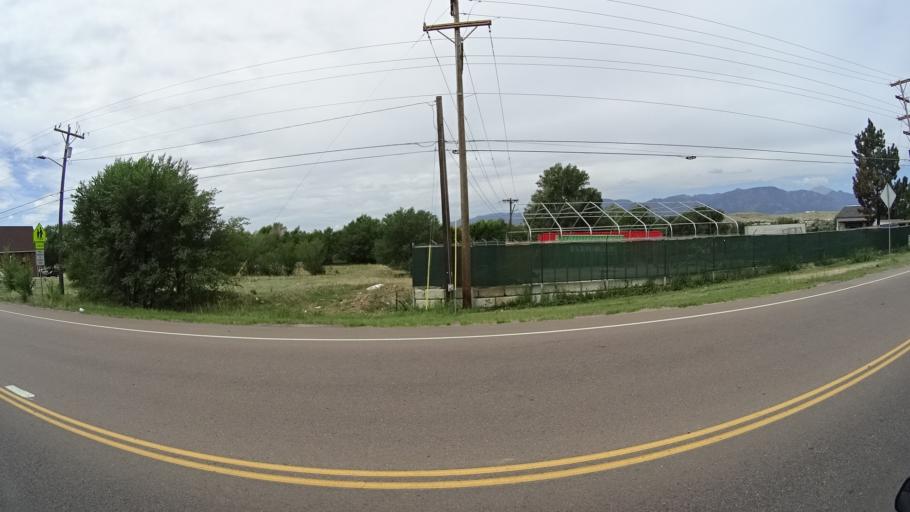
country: US
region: Colorado
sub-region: El Paso County
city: Fountain
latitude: 38.6976
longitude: -104.7059
